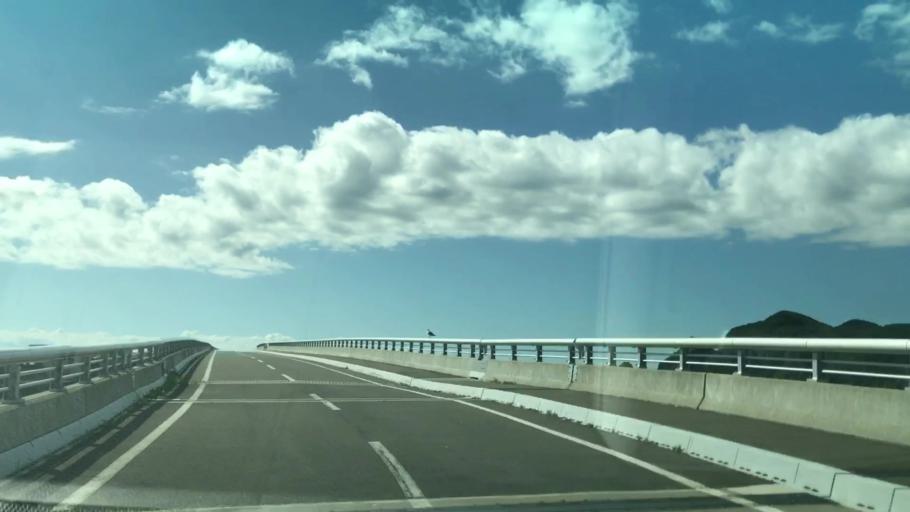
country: JP
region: Hokkaido
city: Muroran
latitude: 42.3100
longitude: 140.9655
